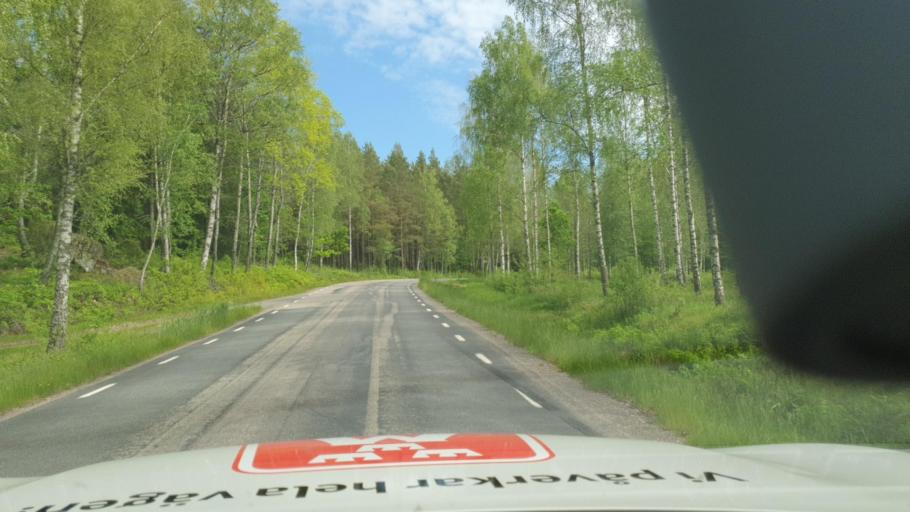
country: SE
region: Vaestra Goetaland
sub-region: Alingsas Kommun
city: Sollebrunn
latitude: 58.2111
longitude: 12.5472
